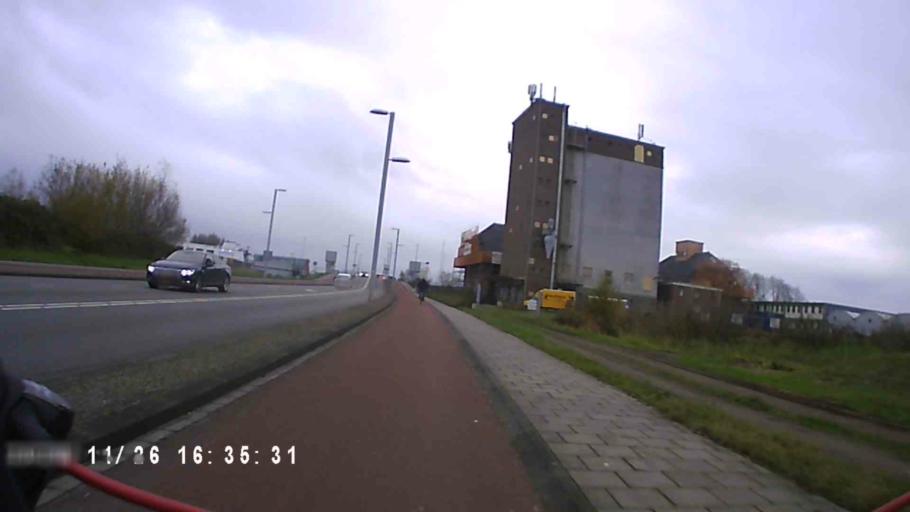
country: NL
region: Groningen
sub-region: Gemeente Groningen
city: Oosterpark
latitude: 53.2213
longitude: 6.5896
